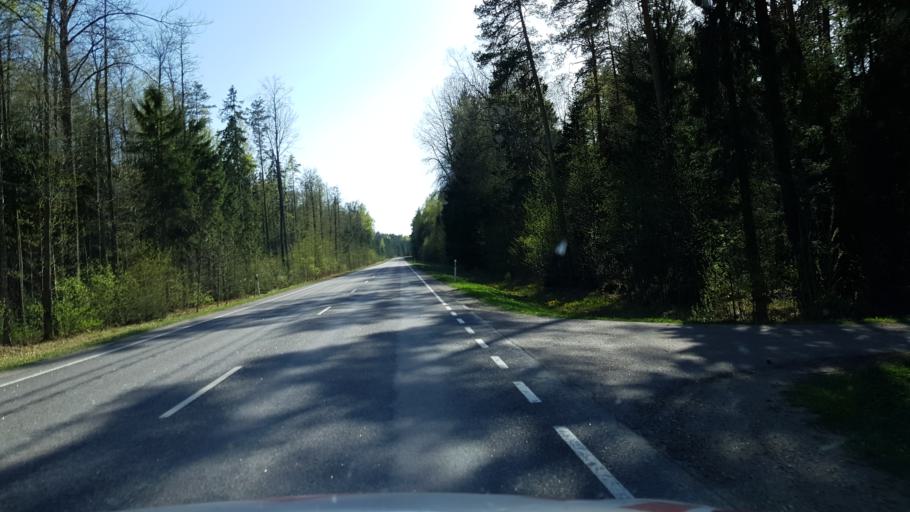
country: EE
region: Viljandimaa
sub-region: Moisakuela linn
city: Moisakula
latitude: 58.2290
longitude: 25.1130
